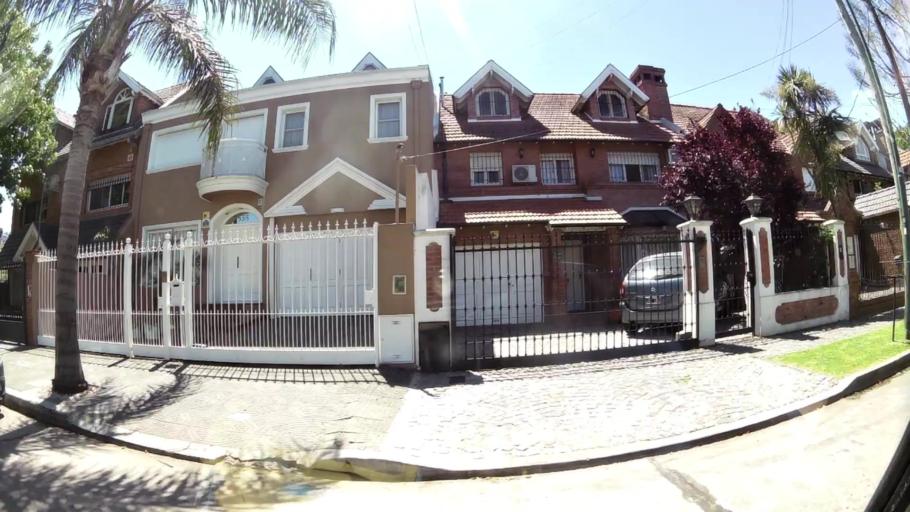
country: AR
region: Buenos Aires
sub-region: Partido de San Isidro
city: San Isidro
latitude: -34.4852
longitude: -58.5121
